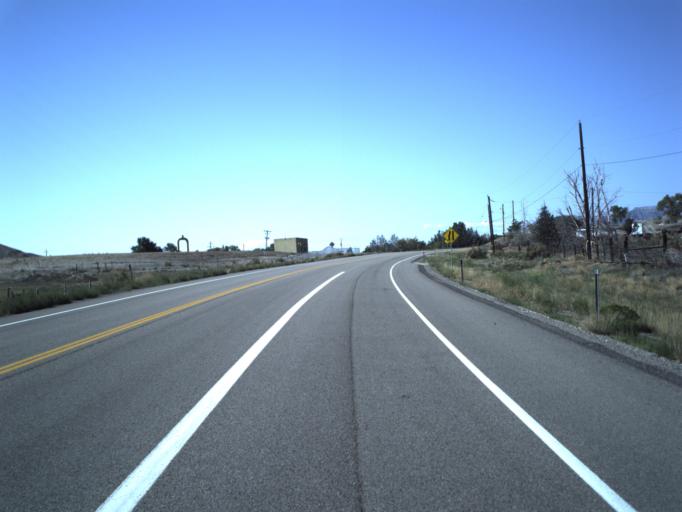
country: US
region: Utah
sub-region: Emery County
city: Ferron
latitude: 39.1316
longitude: -111.1008
